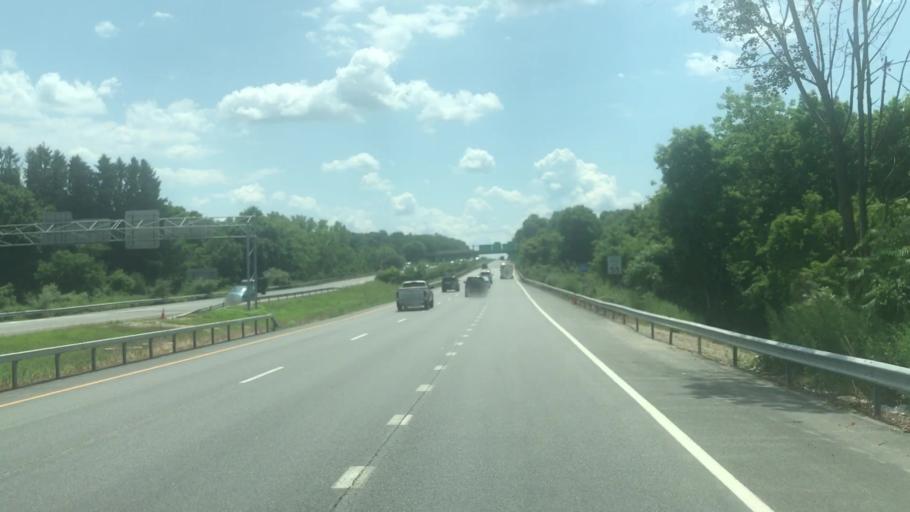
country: US
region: New York
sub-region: Putnam County
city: Brewster
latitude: 41.3964
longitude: -73.5954
